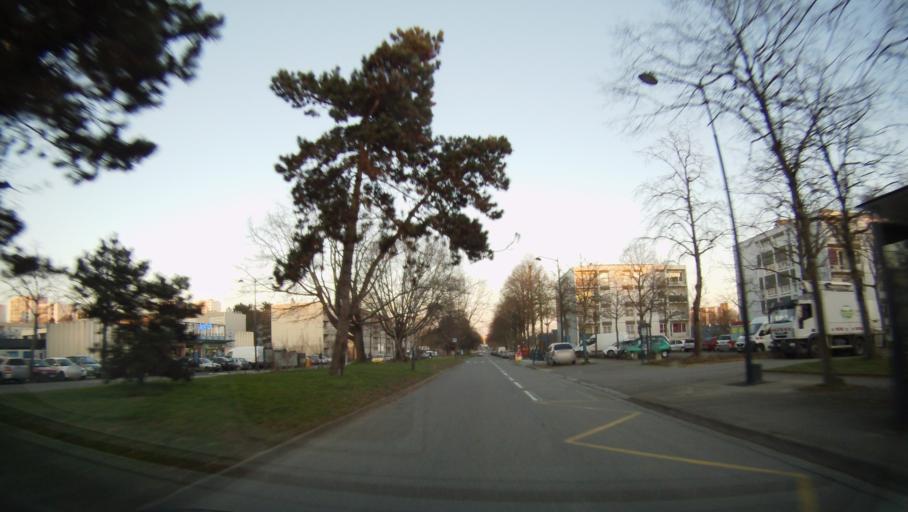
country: FR
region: Brittany
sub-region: Departement d'Ille-et-Vilaine
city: Rennes
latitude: 48.0846
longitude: -1.6581
